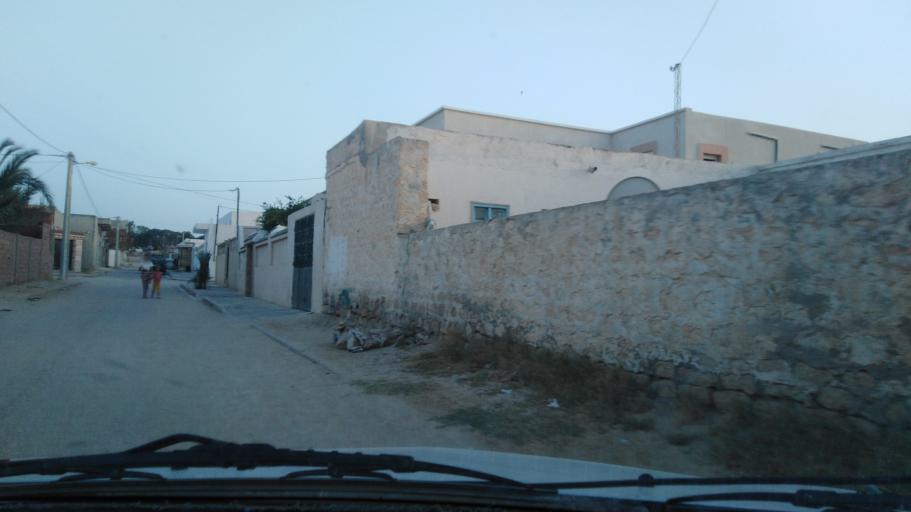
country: TN
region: Qabis
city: Gabes
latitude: 33.9543
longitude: 9.9976
